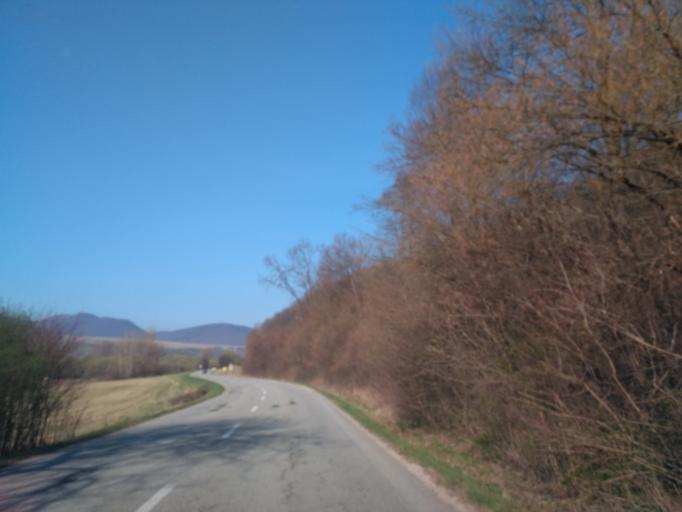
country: SK
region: Kosicky
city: Medzev
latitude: 48.6960
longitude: 20.9244
